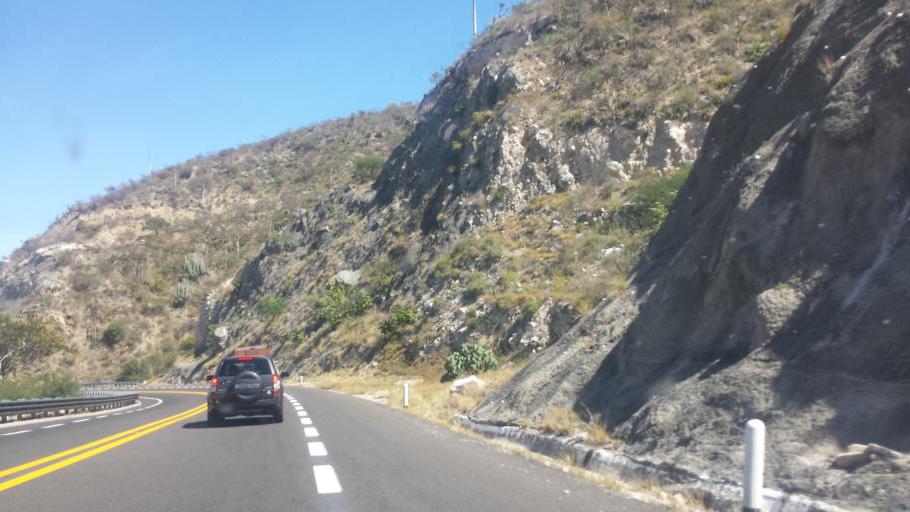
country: MX
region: Puebla
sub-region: San Jose Miahuatlan
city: San Pedro Tetitlan
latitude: 18.1388
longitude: -97.3186
